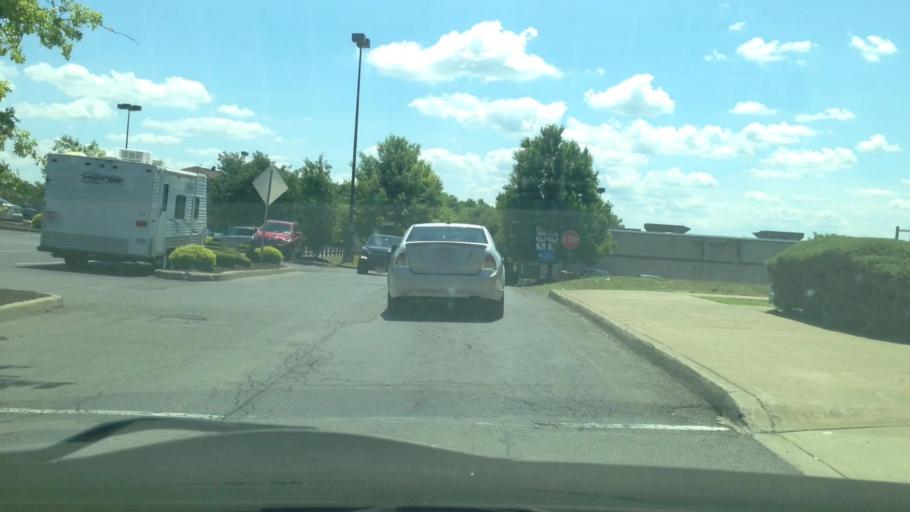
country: US
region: New York
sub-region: Ulster County
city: Lake Katrine
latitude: 41.9725
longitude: -73.9876
